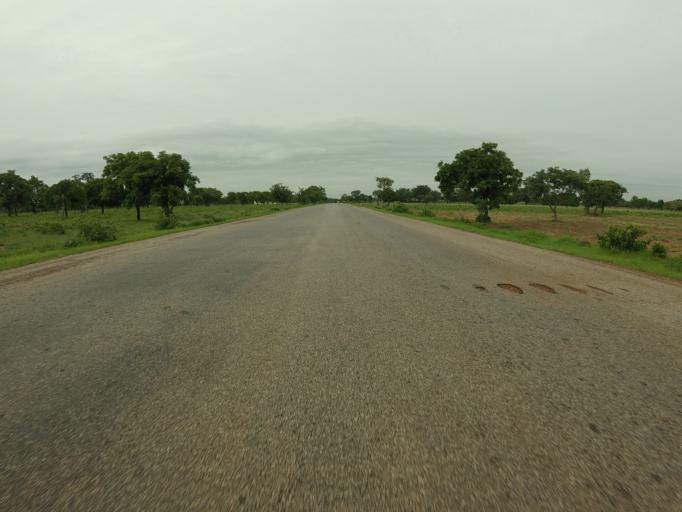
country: GH
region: Northern
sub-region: Yendi
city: Yendi
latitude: 9.5106
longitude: -0.0281
